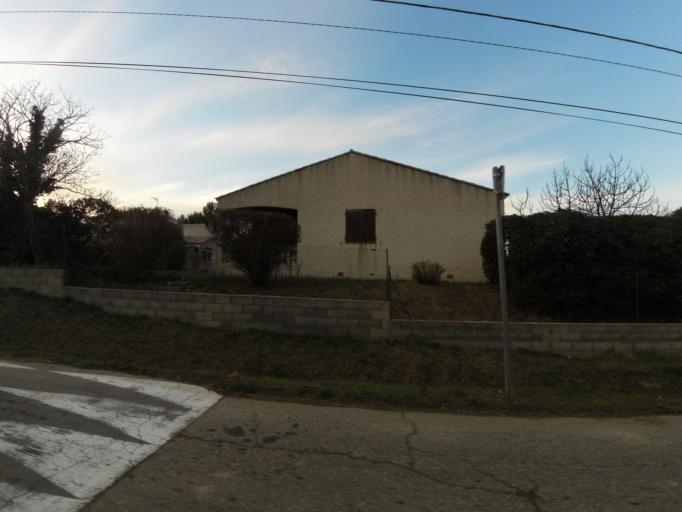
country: FR
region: Languedoc-Roussillon
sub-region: Departement du Gard
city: Calvisson
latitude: 43.7905
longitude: 4.2020
